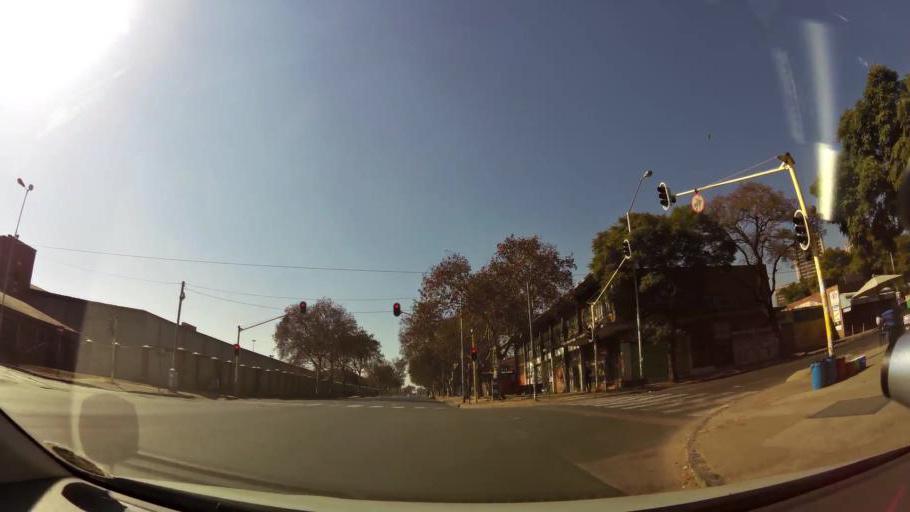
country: ZA
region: Gauteng
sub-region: City of Tshwane Metropolitan Municipality
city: Pretoria
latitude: -25.7396
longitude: 28.1825
